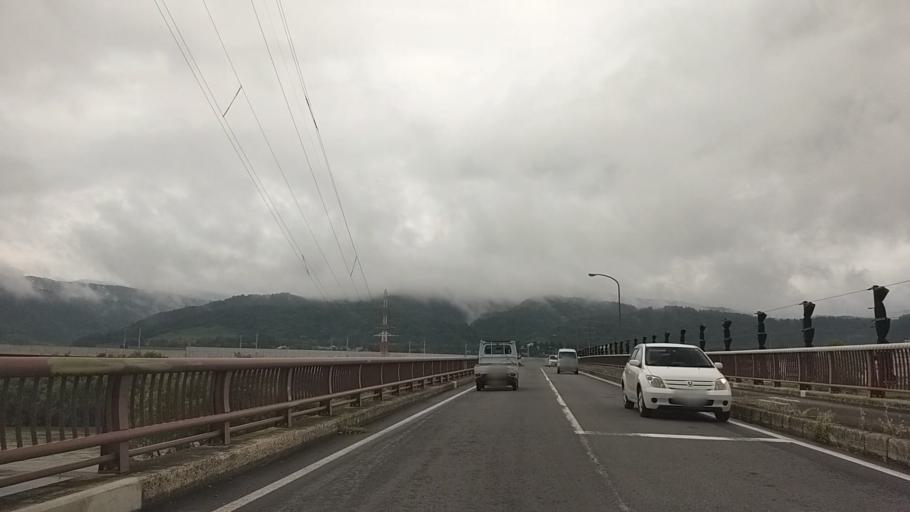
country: JP
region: Nagano
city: Iiyama
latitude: 36.8409
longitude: 138.3662
